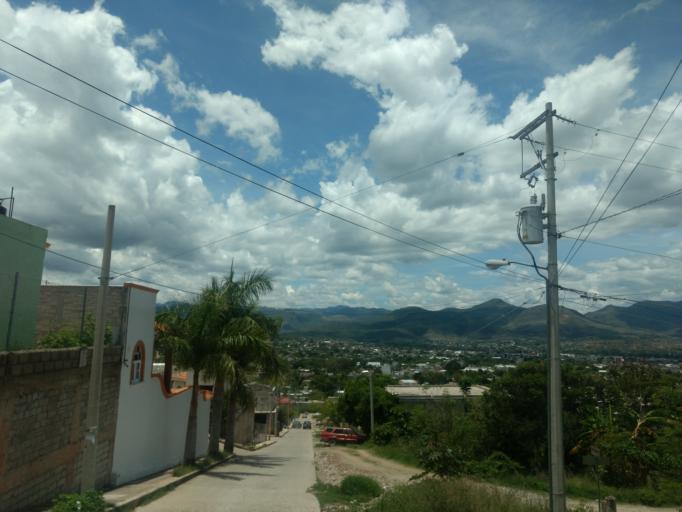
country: MX
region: Oaxaca
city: Ciudad de Huajuapam de Leon
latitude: 17.8158
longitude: -97.7962
